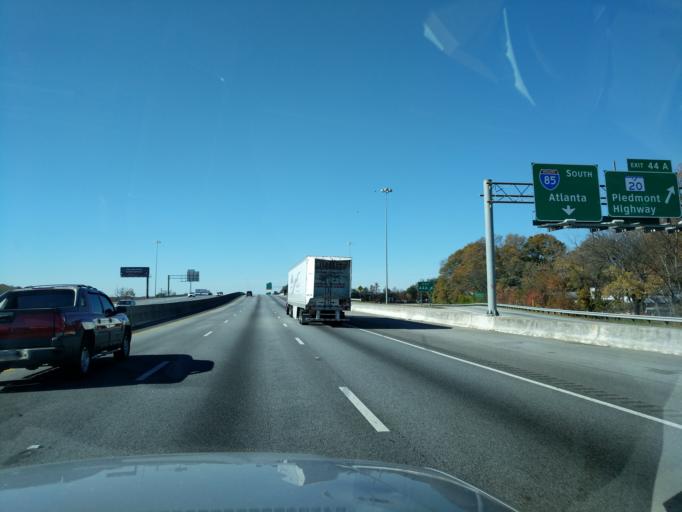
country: US
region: South Carolina
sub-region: Greenville County
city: Gantt
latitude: 34.7911
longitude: -82.4200
